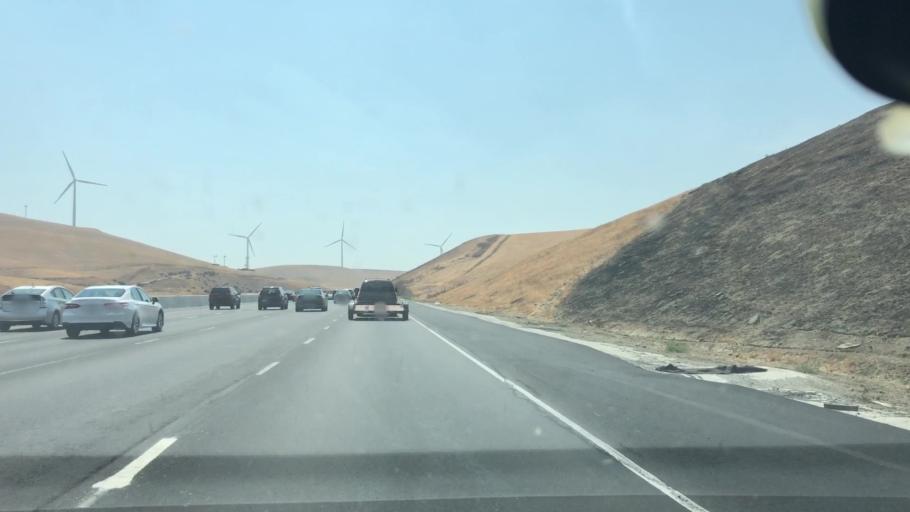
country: US
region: California
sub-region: San Joaquin County
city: Mountain House
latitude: 37.7190
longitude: -121.6485
